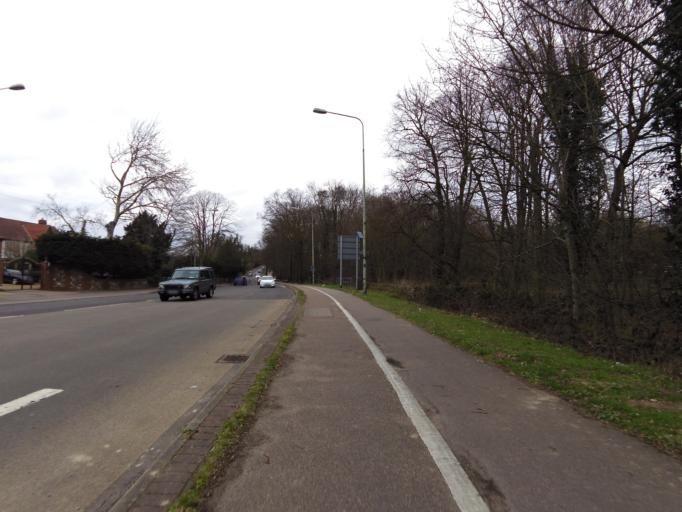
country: GB
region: England
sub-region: Norfolk
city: Hopton on Sea
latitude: 52.5032
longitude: 1.7332
